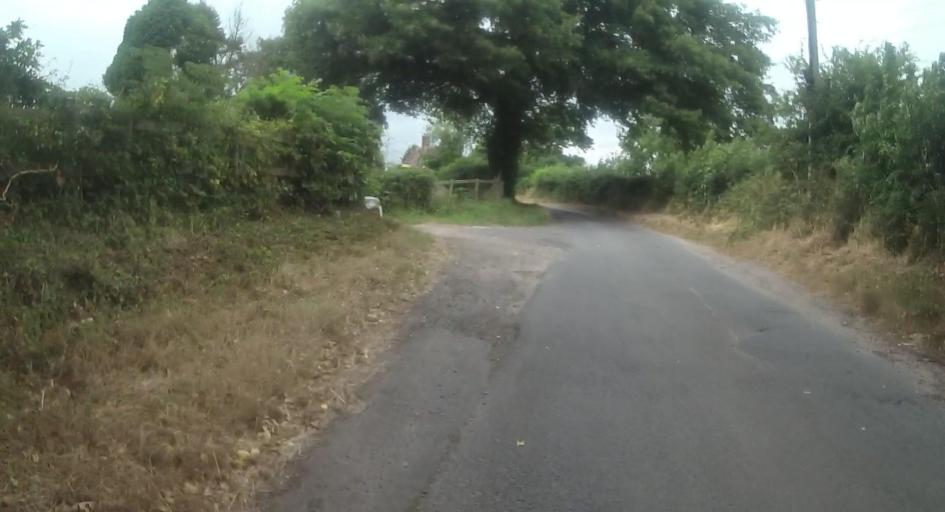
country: GB
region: England
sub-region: Dorset
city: Bovington Camp
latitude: 50.7247
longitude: -2.1935
